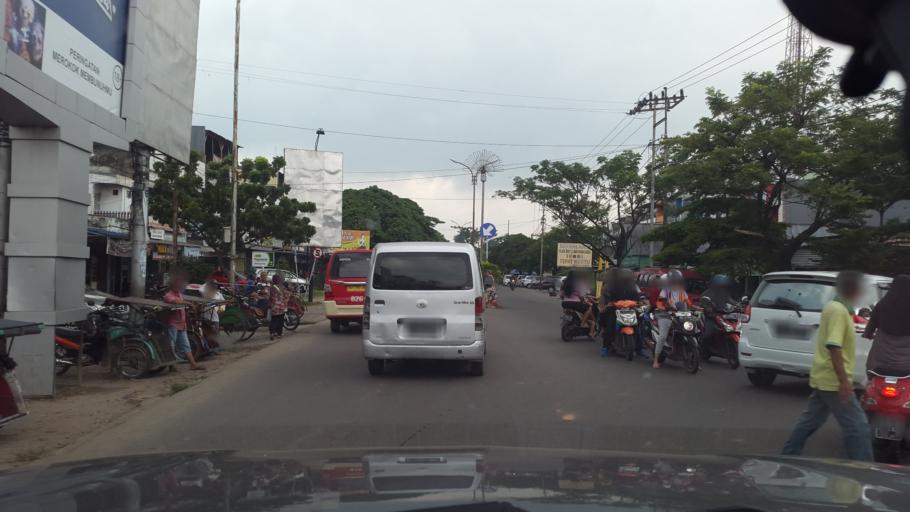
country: ID
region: South Sumatra
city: Plaju
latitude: -2.9957
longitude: 104.8151
